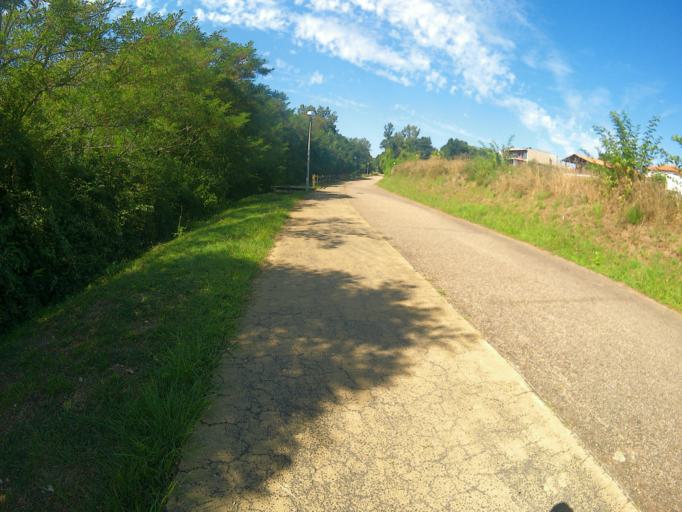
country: PT
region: Viana do Castelo
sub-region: Valenca
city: Valenca
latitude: 42.0143
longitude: -8.6564
